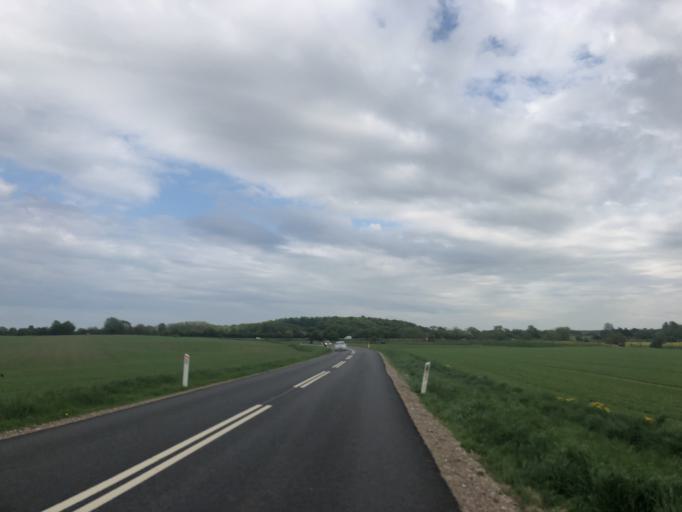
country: DK
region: Zealand
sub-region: Koge Kommune
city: Ejby
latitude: 55.4722
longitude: 12.1190
